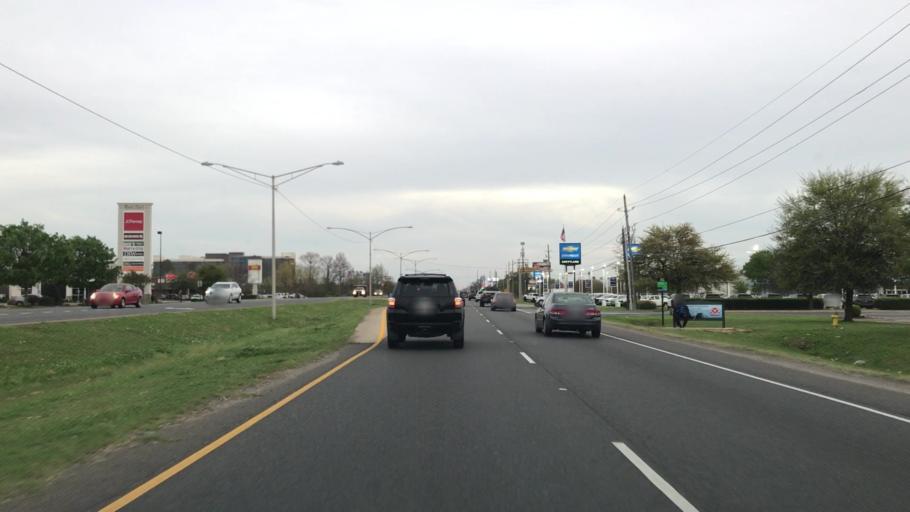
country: US
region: Louisiana
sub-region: Bossier Parish
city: Bossier City
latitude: 32.4381
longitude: -93.7156
